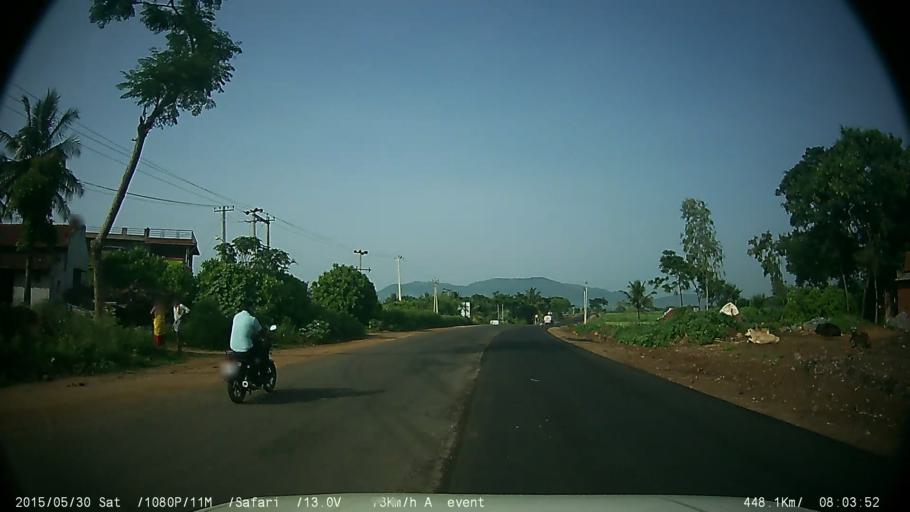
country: IN
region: Karnataka
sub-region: Chamrajnagar
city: Gundlupet
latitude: 11.7903
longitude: 76.6358
